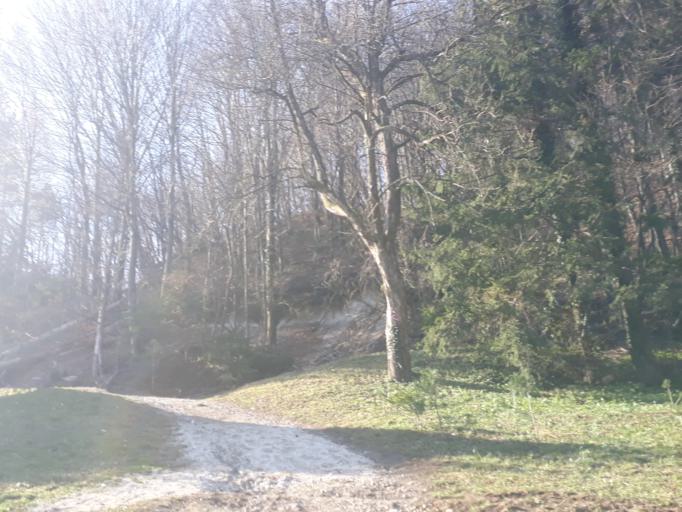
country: HR
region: Varazdinska
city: Ivanec
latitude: 46.1957
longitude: 16.1372
